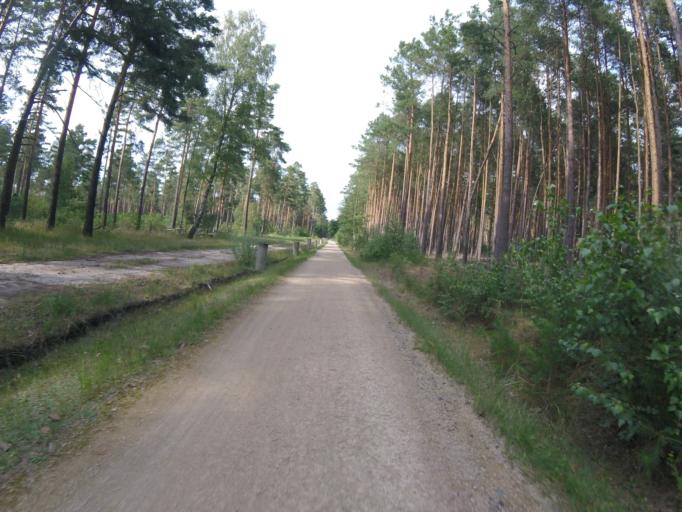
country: DE
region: Brandenburg
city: Halbe
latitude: 52.1719
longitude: 13.7520
